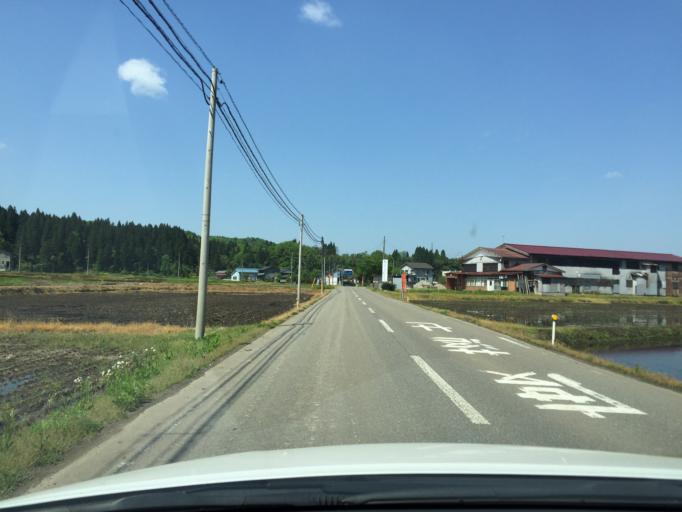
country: JP
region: Niigata
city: Tochio-honcho
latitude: 37.5048
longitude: 139.0601
